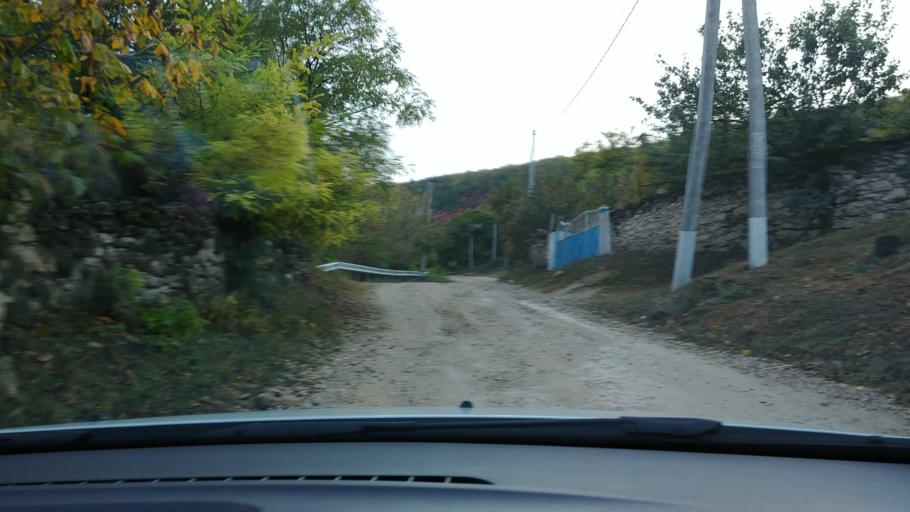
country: MD
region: Rezina
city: Saharna
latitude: 47.6892
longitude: 28.9753
